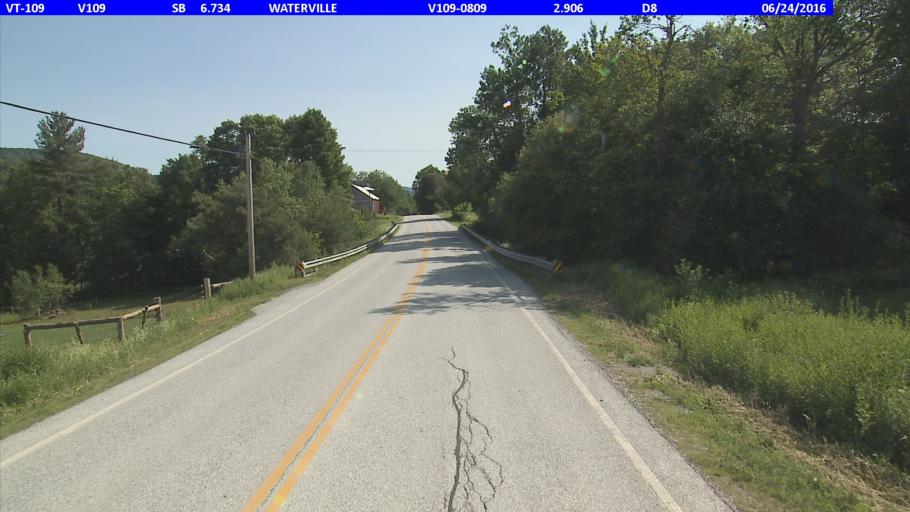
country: US
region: Vermont
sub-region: Lamoille County
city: Johnson
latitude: 44.7197
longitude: -72.7510
